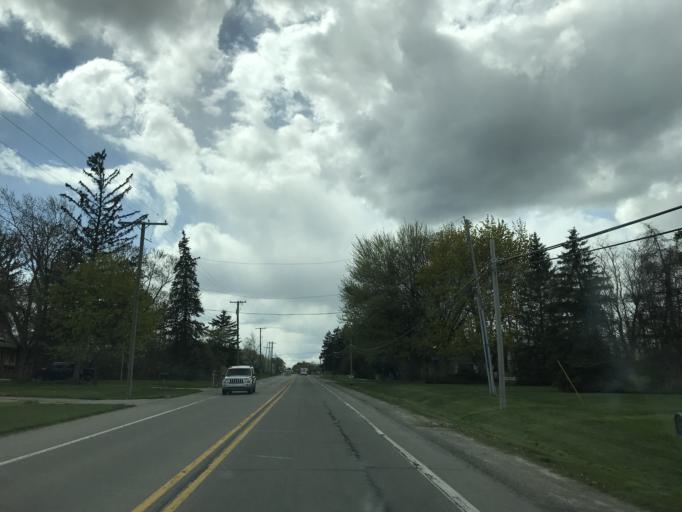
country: US
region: Michigan
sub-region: Wayne County
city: Plymouth
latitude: 42.3778
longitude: -83.5051
